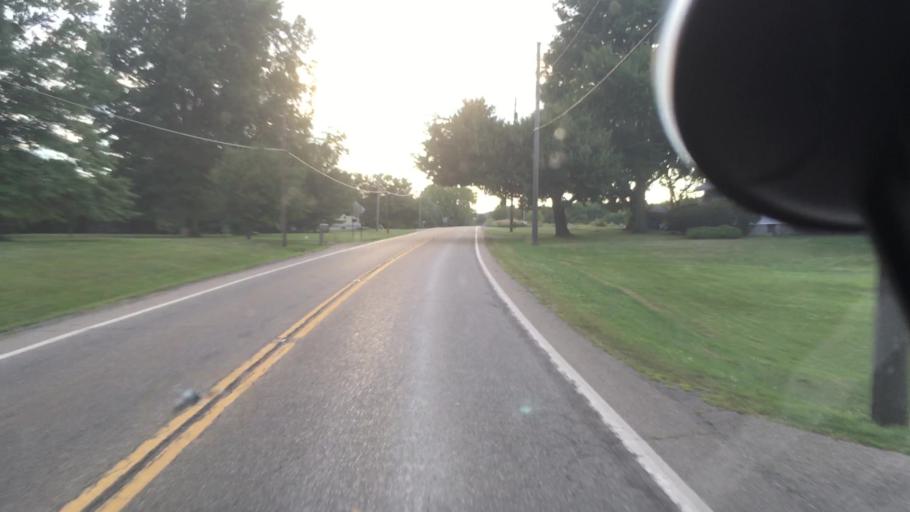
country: US
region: Ohio
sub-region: Columbiana County
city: East Palestine
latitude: 40.8659
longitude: -80.5616
